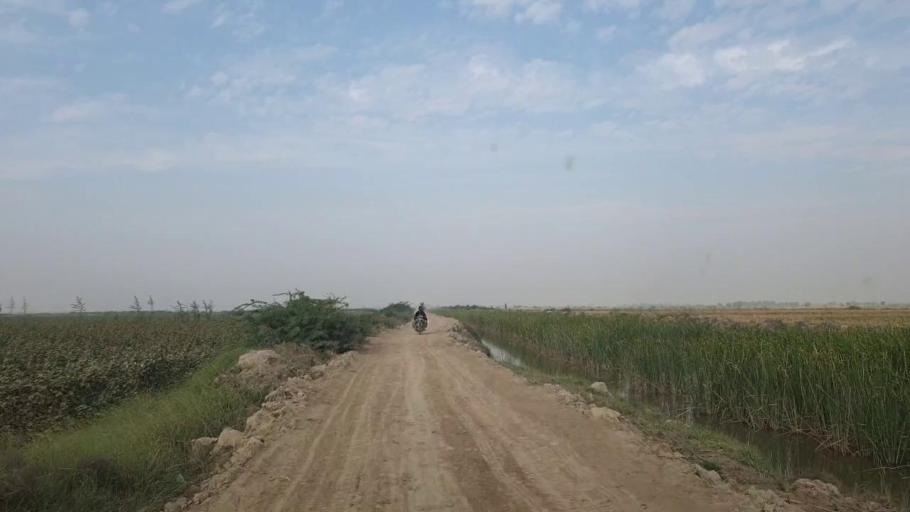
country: PK
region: Sindh
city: Tando Bago
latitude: 24.8642
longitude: 68.9925
